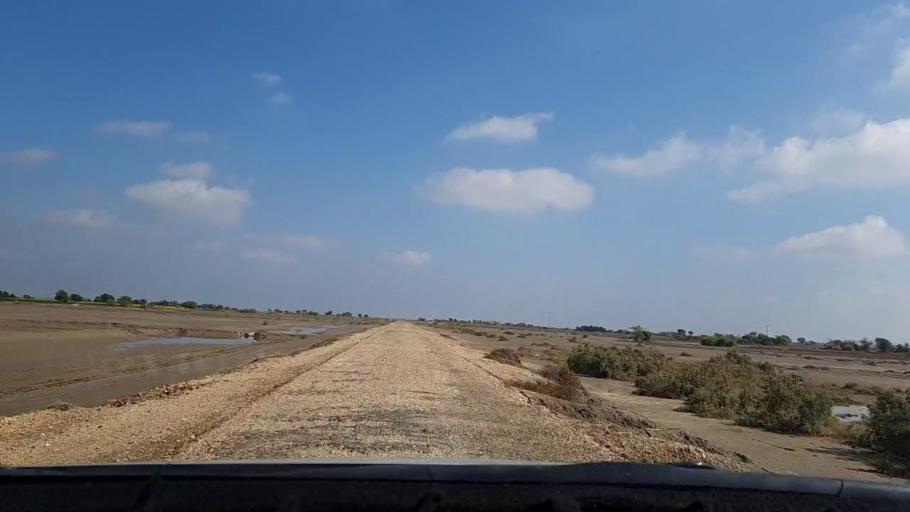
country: PK
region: Sindh
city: Pithoro
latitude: 25.7370
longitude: 69.2650
